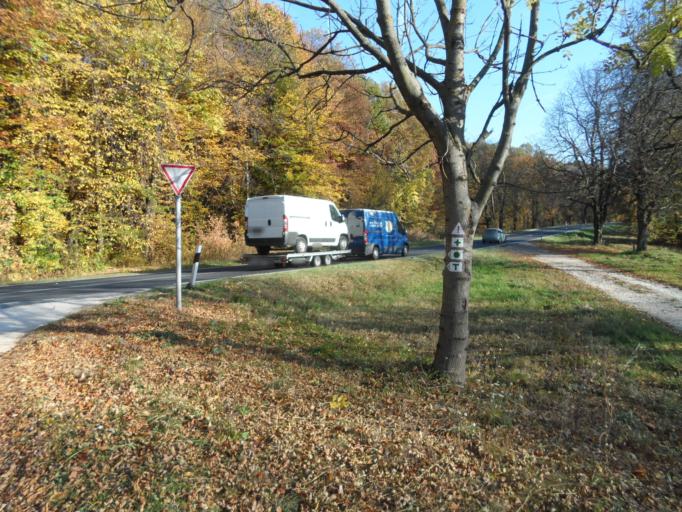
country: HU
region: Veszprem
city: Urkut
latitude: 47.1909
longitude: 17.6431
